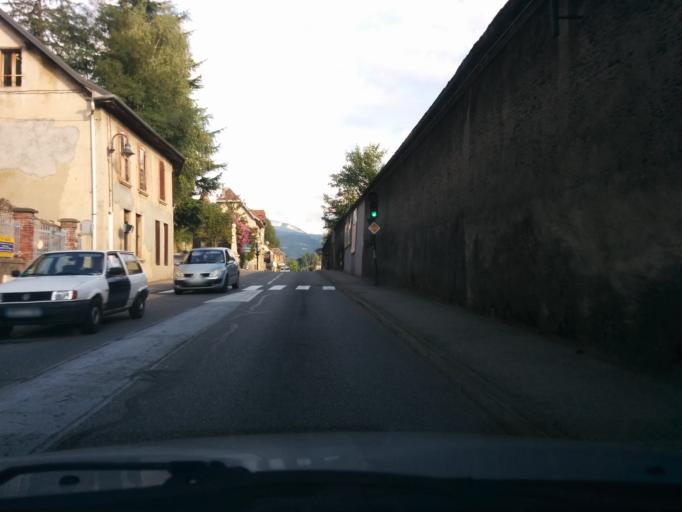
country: FR
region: Rhone-Alpes
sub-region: Departement de la Savoie
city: Le Pont-de-Beauvoisin
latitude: 45.5338
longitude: 5.6771
